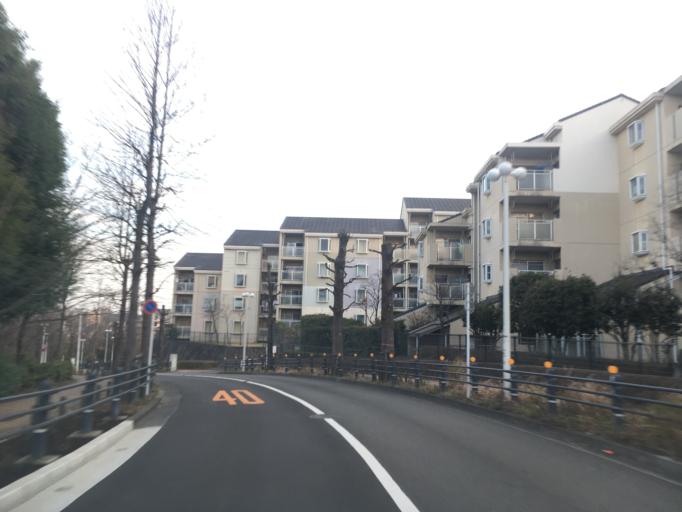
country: JP
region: Tokyo
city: Hino
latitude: 35.6158
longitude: 139.3998
